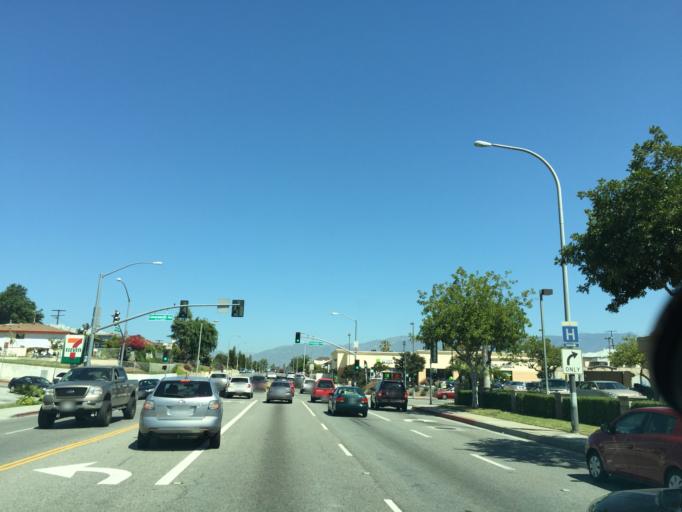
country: US
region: California
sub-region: Los Angeles County
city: Alhambra
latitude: 34.0873
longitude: -118.1519
